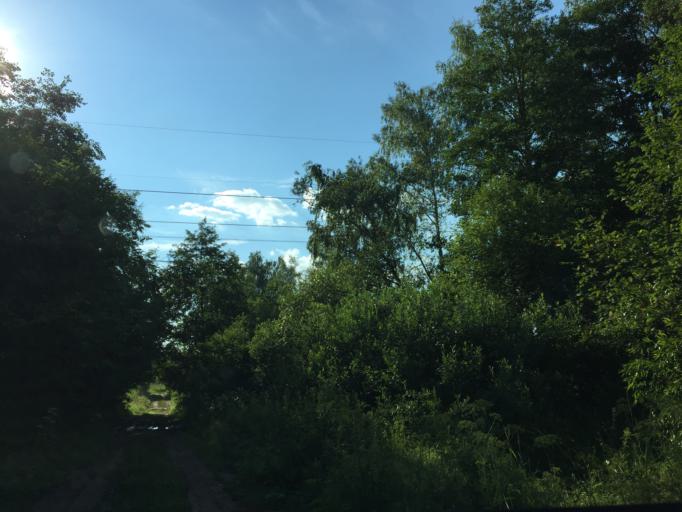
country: LV
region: Krimulda
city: Ragana
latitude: 57.1447
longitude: 24.7630
